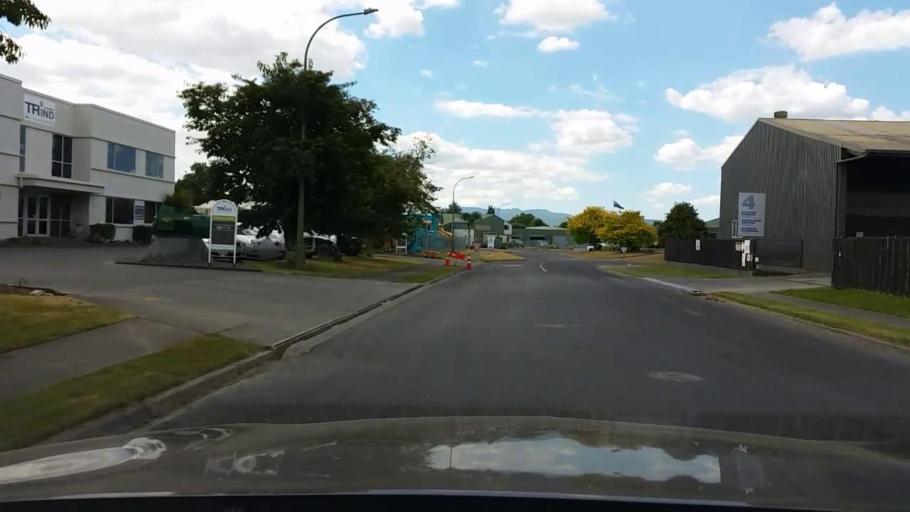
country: NZ
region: Waikato
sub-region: Matamata-Piako District
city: Matamata
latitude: -37.8148
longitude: 175.7895
